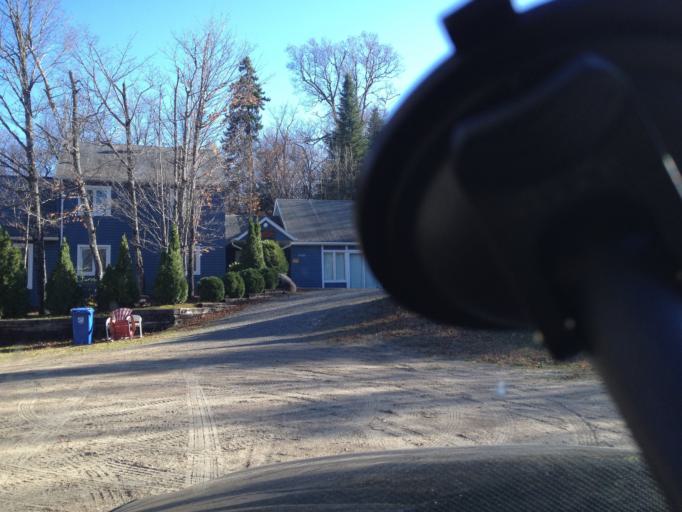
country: CA
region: Quebec
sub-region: Laurentides
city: Val-David
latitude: 46.2945
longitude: -74.1108
